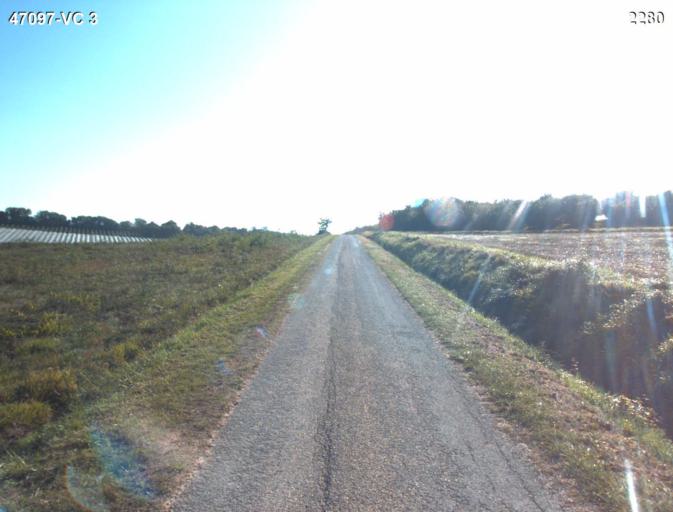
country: FR
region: Aquitaine
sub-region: Departement du Lot-et-Garonne
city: Vianne
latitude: 44.1929
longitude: 0.3431
